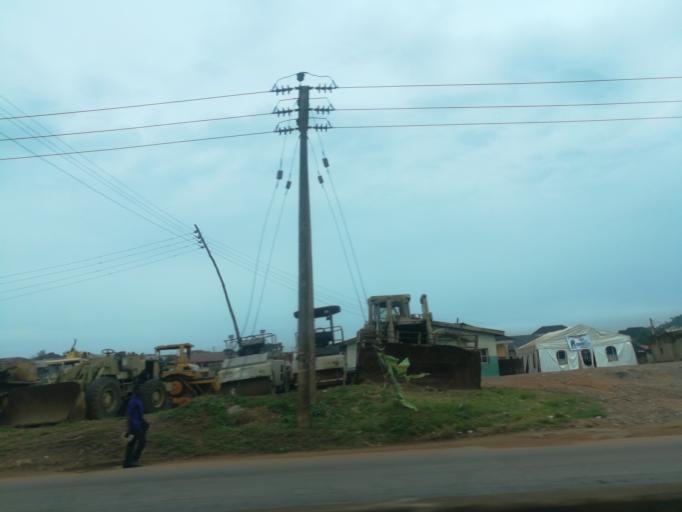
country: NG
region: Oyo
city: Egbeda
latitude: 7.3874
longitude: 3.9825
